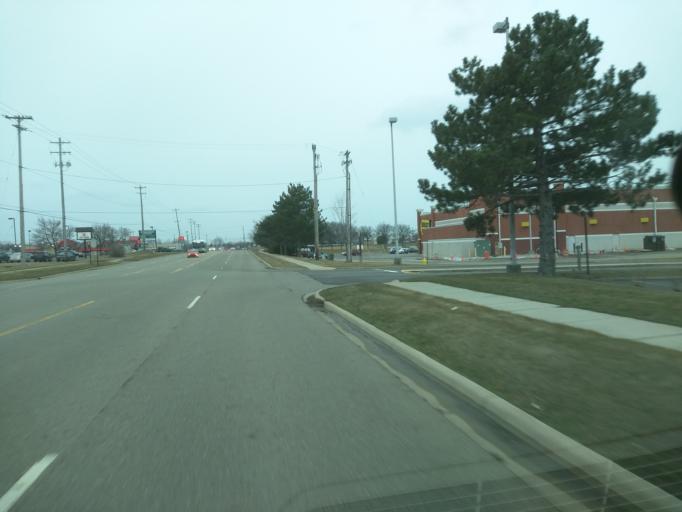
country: US
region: Michigan
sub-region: Eaton County
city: Waverly
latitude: 42.7445
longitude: -84.6225
